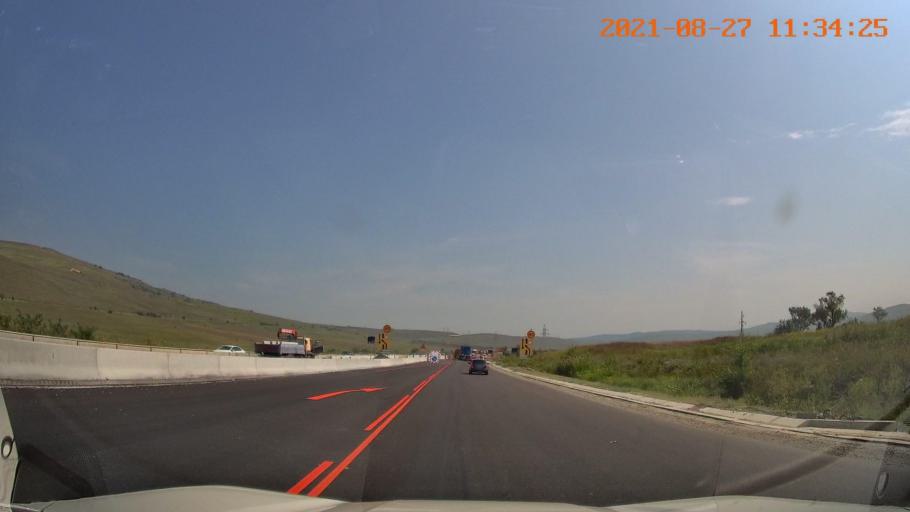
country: RU
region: Stavropol'skiy
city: Barsukovskaya
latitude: 44.8244
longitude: 41.8845
